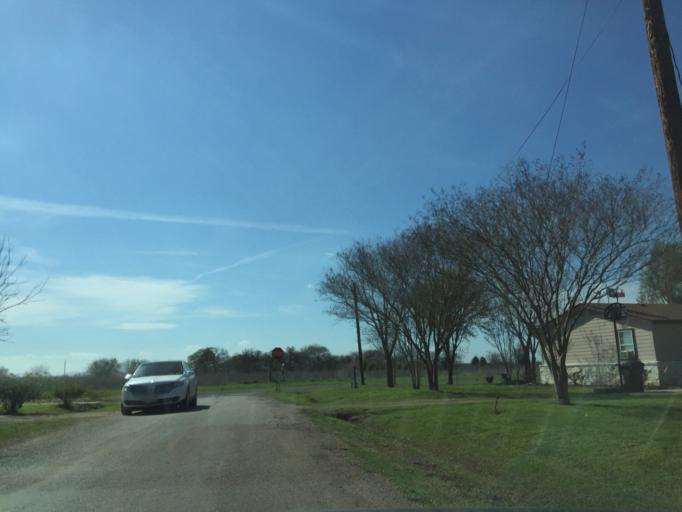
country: US
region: Texas
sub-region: Milam County
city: Thorndale
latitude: 30.5802
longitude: -97.1849
